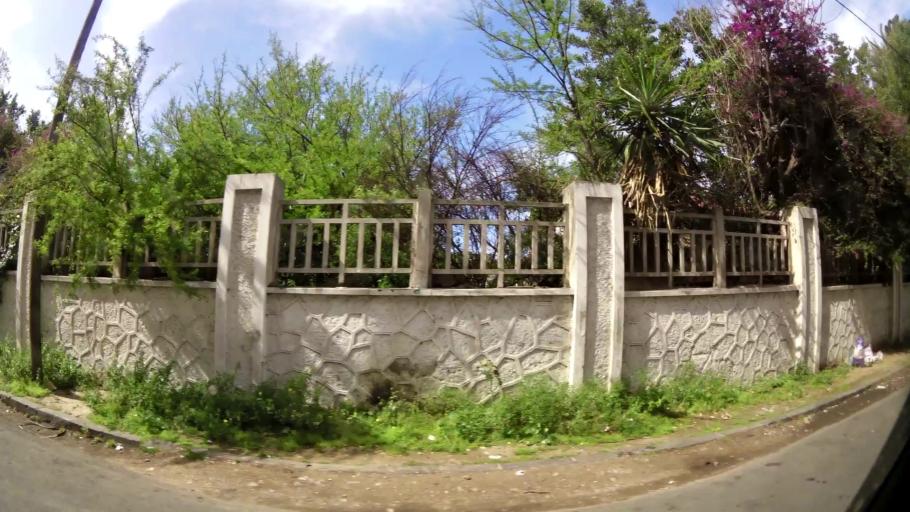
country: MA
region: Grand Casablanca
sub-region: Casablanca
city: Casablanca
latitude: 33.5861
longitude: -7.5861
